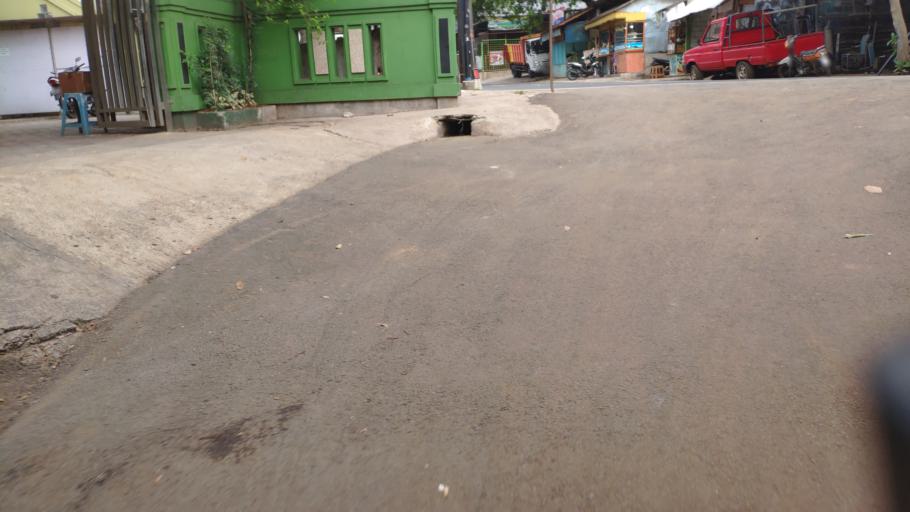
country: ID
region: West Java
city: Depok
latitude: -6.3215
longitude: 106.8248
